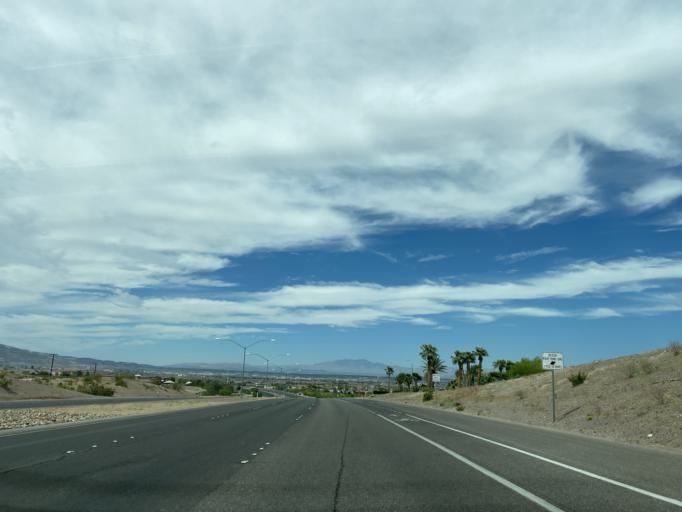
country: US
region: Nevada
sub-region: Clark County
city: Henderson
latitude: 36.0766
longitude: -114.9466
